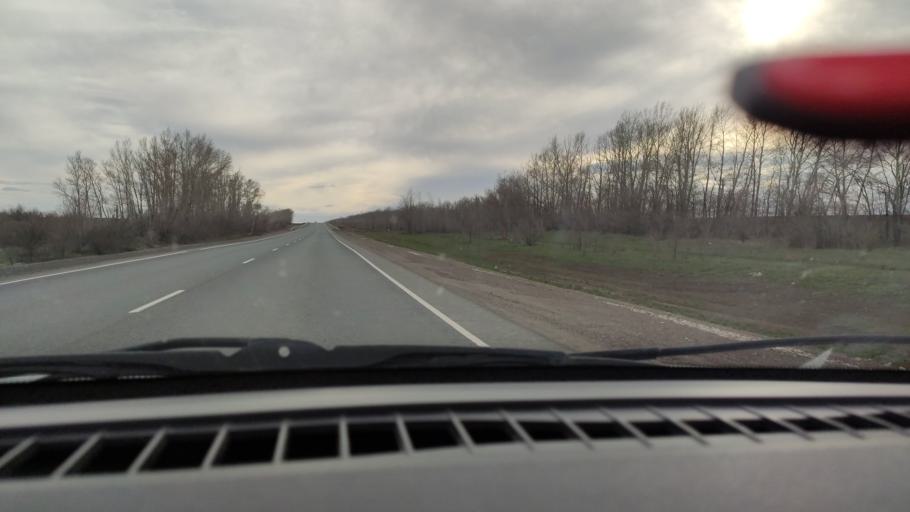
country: RU
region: Orenburg
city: Sakmara
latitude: 52.3064
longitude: 55.4457
